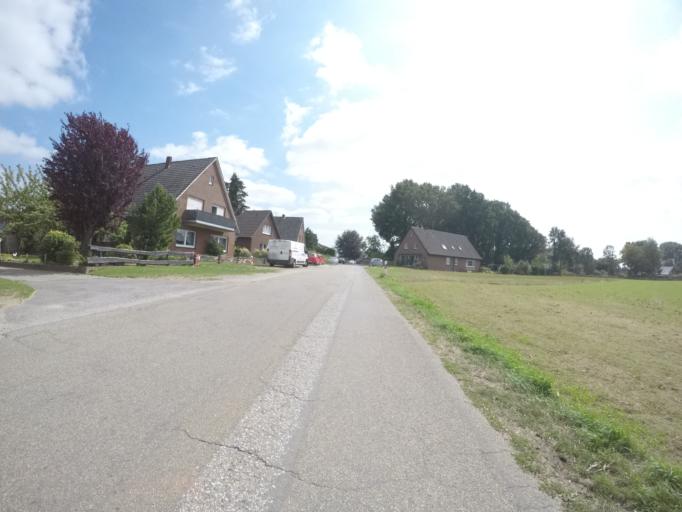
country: DE
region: North Rhine-Westphalia
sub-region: Regierungsbezirk Munster
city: Isselburg
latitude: 51.8135
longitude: 6.4562
